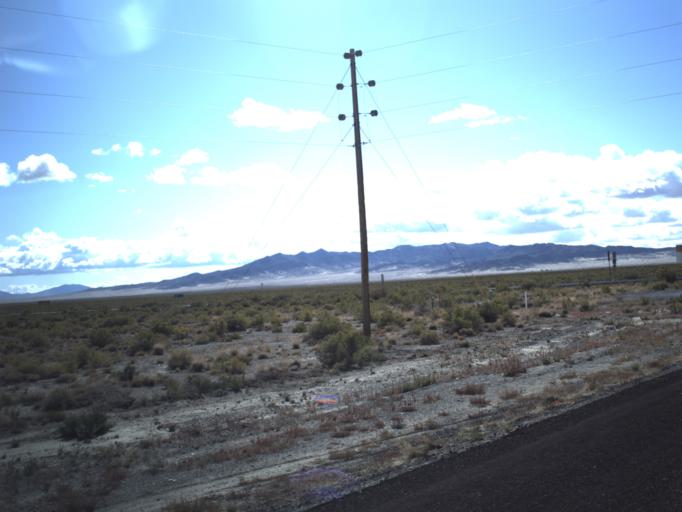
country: US
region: Nevada
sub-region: White Pine County
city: McGill
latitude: 39.0571
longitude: -114.0366
